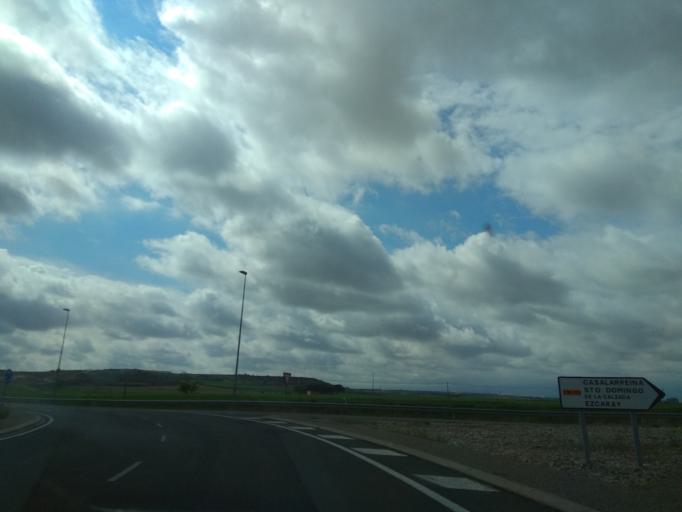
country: ES
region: La Rioja
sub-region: Provincia de La Rioja
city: Casalarreina
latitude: 42.5545
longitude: -2.8987
